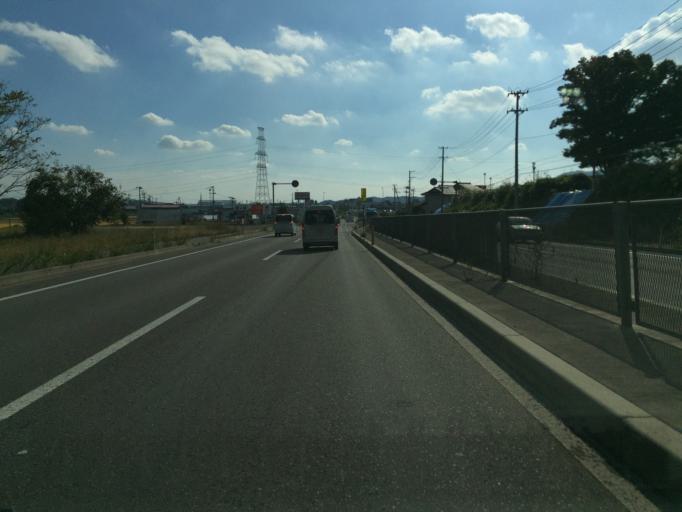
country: JP
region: Fukushima
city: Motomiya
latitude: 37.5473
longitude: 140.3993
